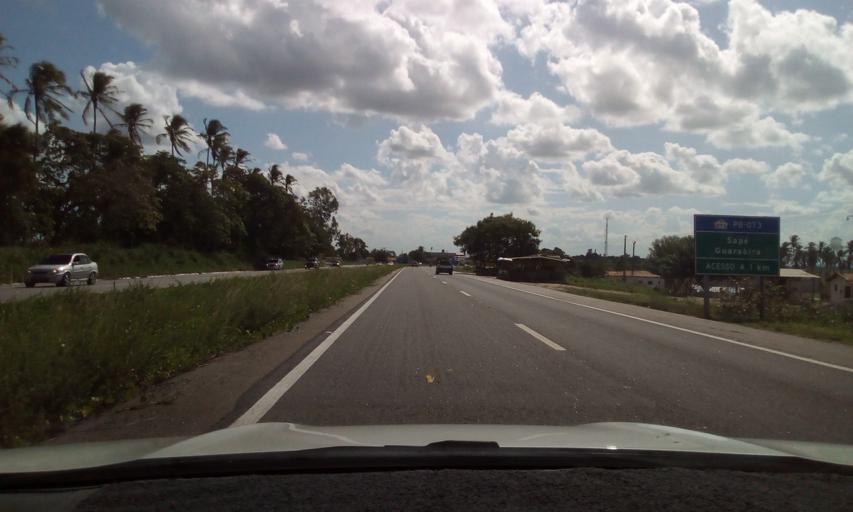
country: BR
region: Paraiba
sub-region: Pilar
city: Pilar
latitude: -7.1909
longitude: -35.2203
